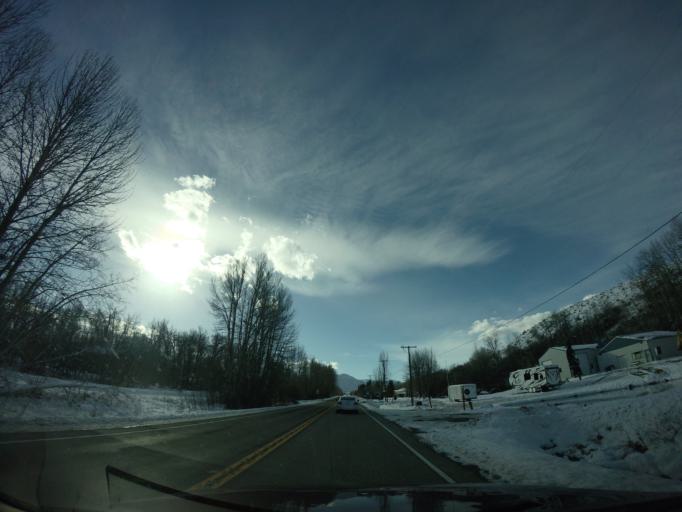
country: US
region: Montana
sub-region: Carbon County
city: Red Lodge
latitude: 45.2208
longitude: -109.2409
